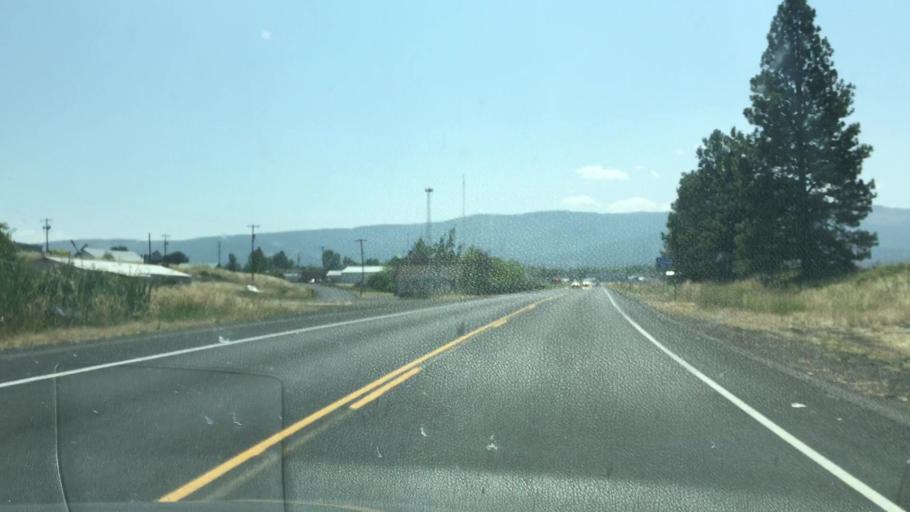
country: US
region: Idaho
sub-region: Idaho County
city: Grangeville
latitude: 45.9341
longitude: -116.1330
